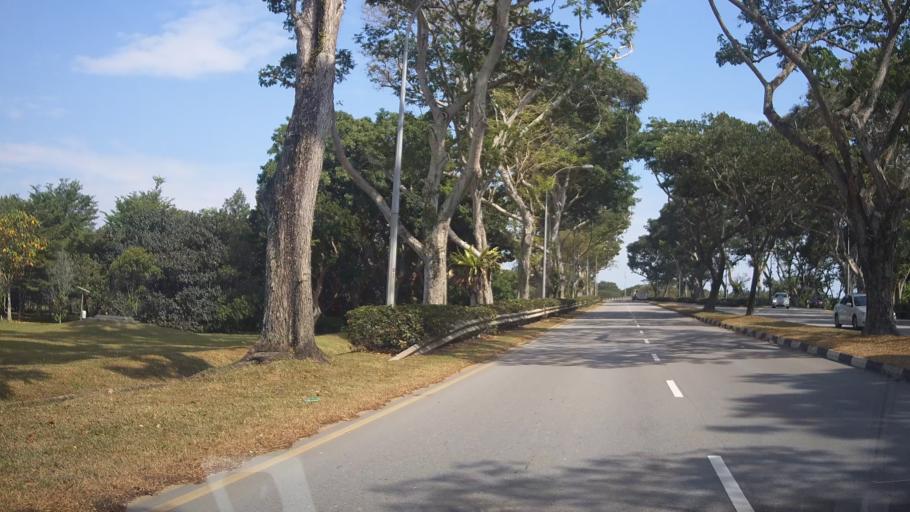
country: SG
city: Singapore
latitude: 1.3258
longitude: 103.9697
